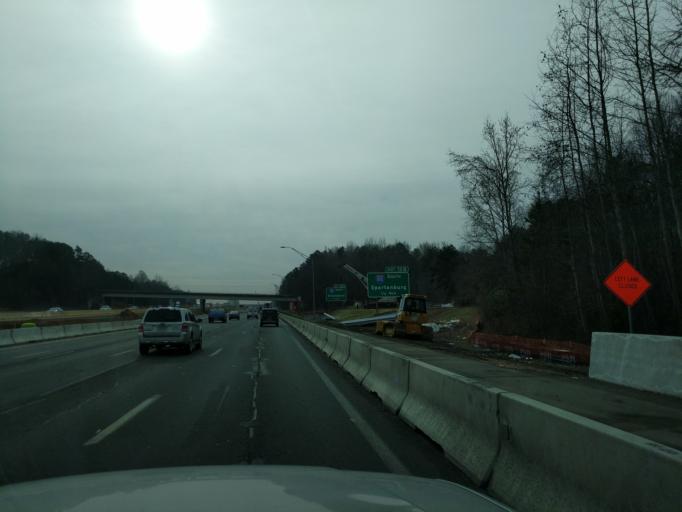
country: US
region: North Carolina
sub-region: Mecklenburg County
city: Charlotte
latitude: 35.2862
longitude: -80.8497
